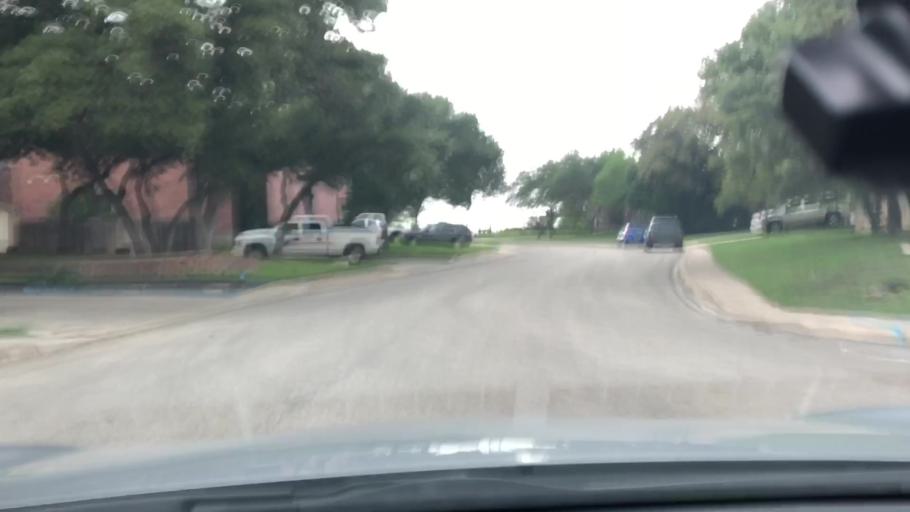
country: US
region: Texas
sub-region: Bexar County
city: Leon Valley
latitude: 29.5049
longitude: -98.6766
